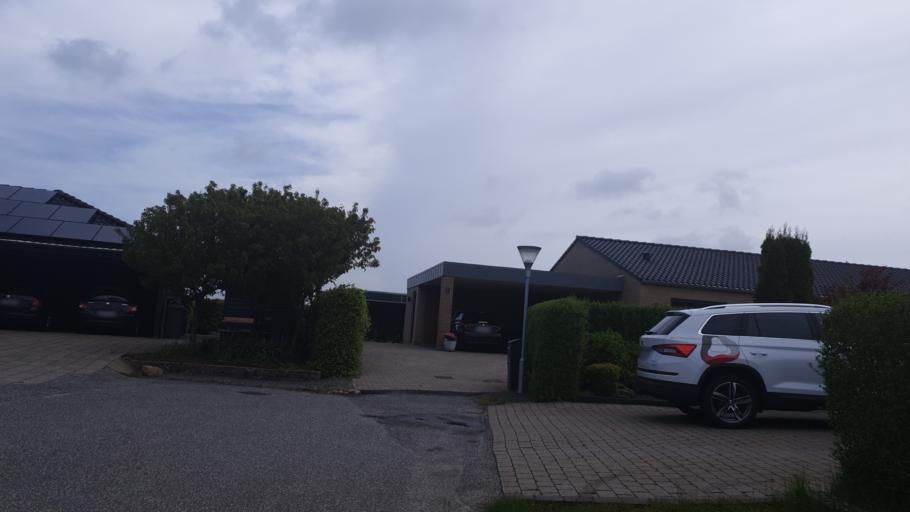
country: DK
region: Central Jutland
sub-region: Hedensted Kommune
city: Hedensted
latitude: 55.8127
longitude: 9.7015
